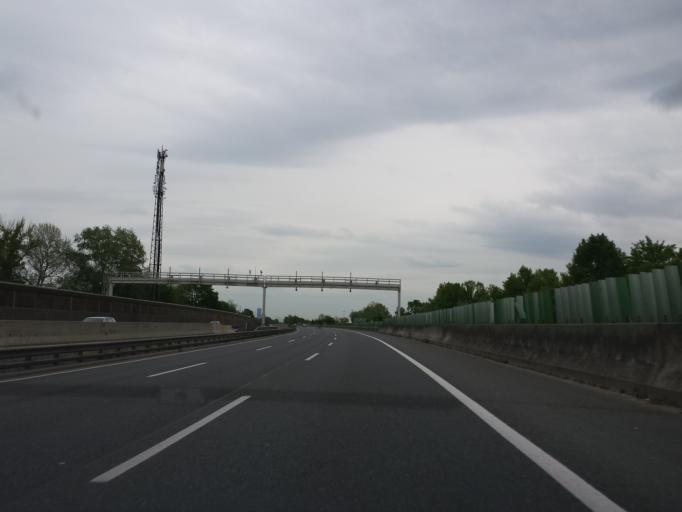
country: AT
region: Lower Austria
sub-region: Politischer Bezirk Korneuburg
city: Langenzersdorf
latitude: 48.3033
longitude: 16.3462
